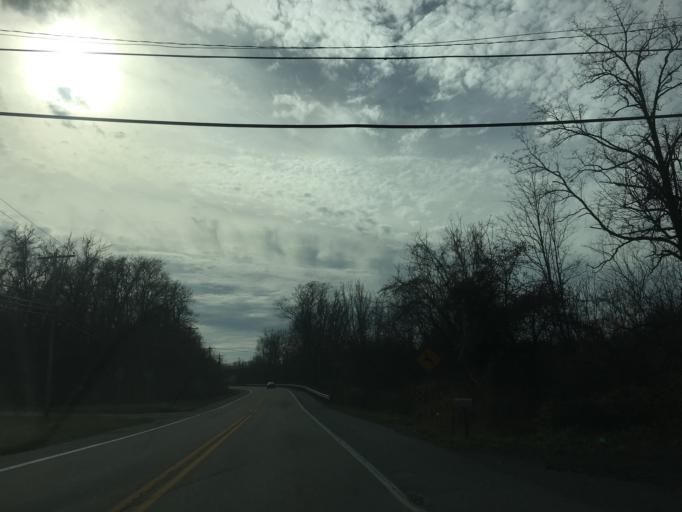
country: US
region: Pennsylvania
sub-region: Dauphin County
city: Colonial Park
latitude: 40.3118
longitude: -76.8226
